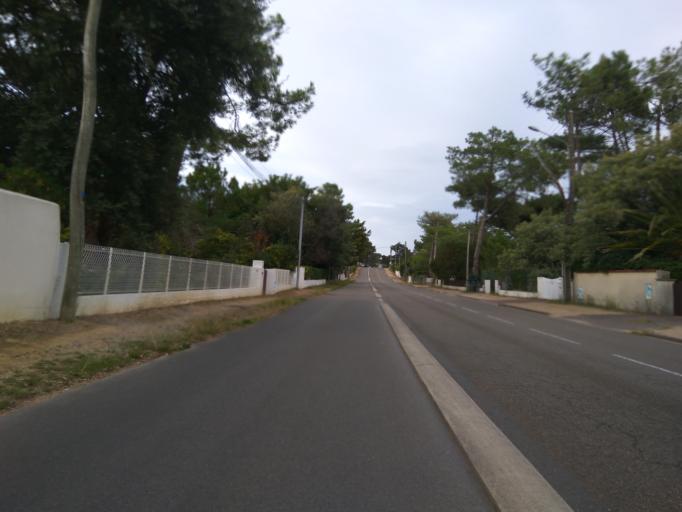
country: FR
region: Aquitaine
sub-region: Departement des Landes
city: Capbreton
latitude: 43.6420
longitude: -1.4416
